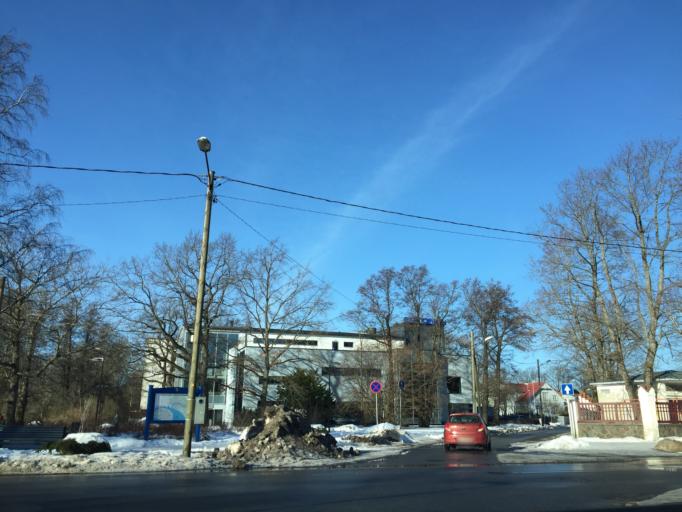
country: EE
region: Paernumaa
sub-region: Paernu linn
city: Parnu
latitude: 58.3780
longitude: 24.4990
